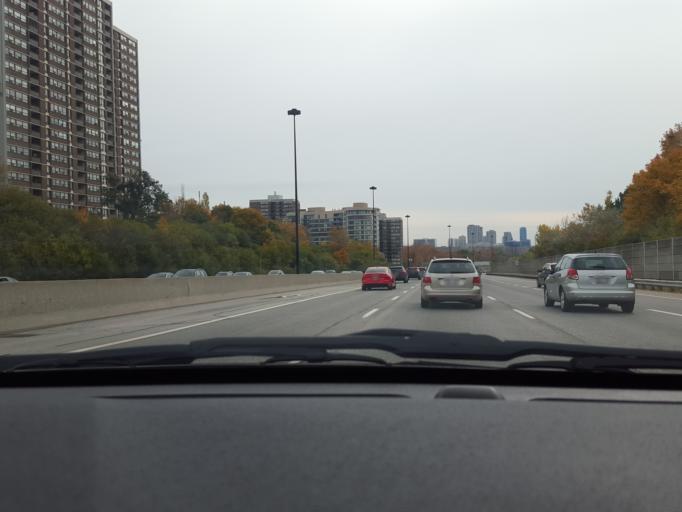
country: CA
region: Ontario
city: Willowdale
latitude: 43.7558
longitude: -79.3351
